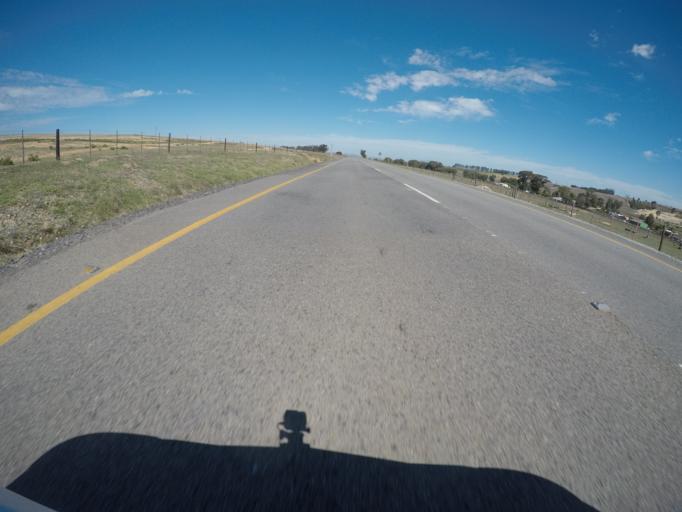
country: ZA
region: Western Cape
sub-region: West Coast District Municipality
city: Malmesbury
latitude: -33.4978
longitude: 18.6807
